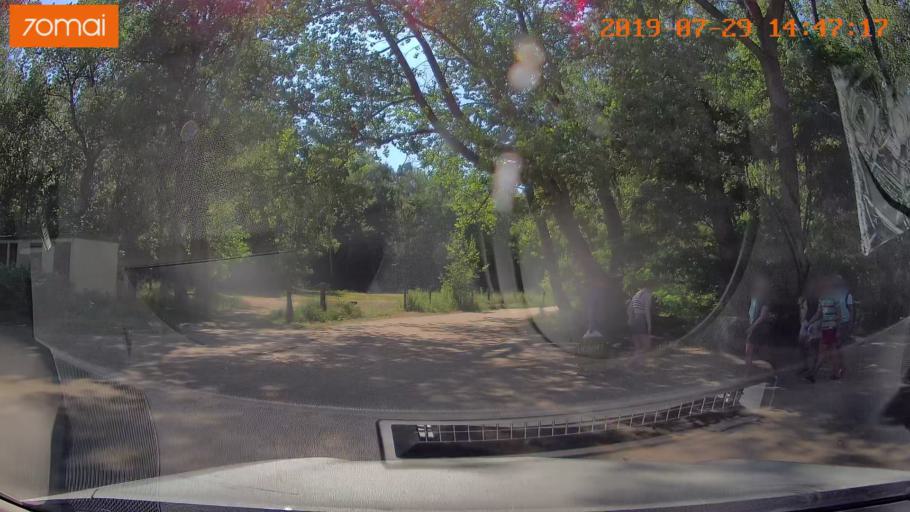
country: RU
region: Kaliningrad
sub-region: Gorod Kaliningrad
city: Baltiysk
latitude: 54.6631
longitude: 19.9012
